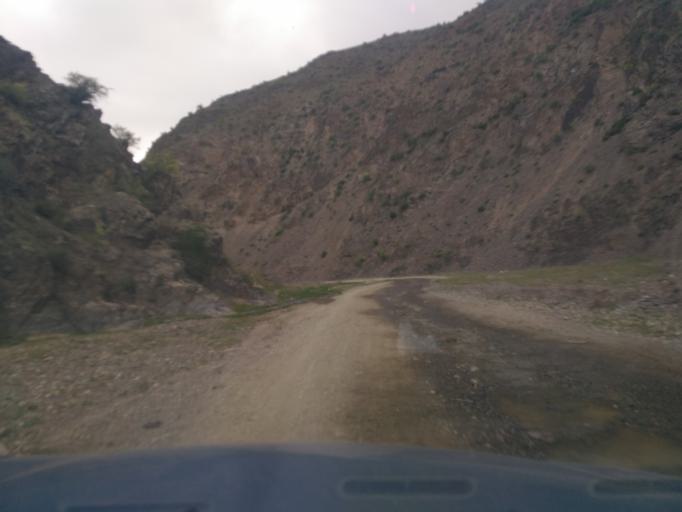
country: UZ
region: Jizzax
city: Zomin
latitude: 39.8538
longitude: 68.3925
